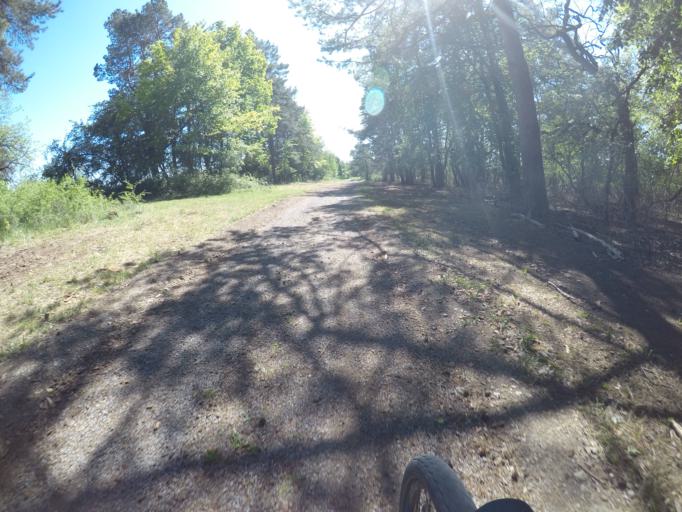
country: DE
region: Baden-Wuerttemberg
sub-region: Karlsruhe Region
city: Heimsheim
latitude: 48.8178
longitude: 8.8716
